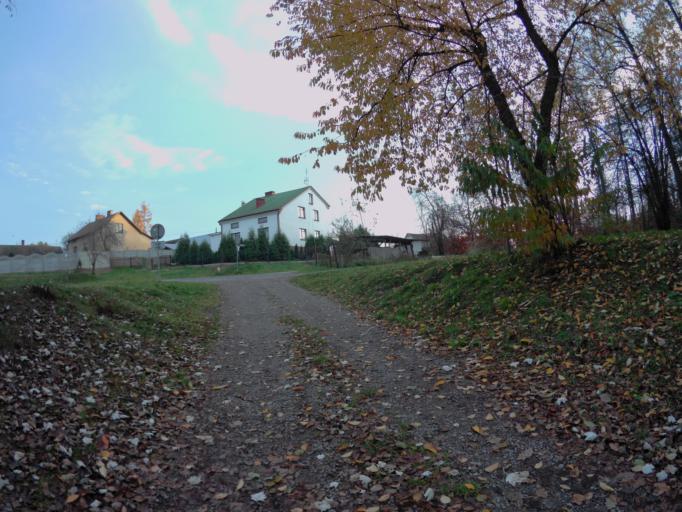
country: PL
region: Subcarpathian Voivodeship
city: Nowa Sarzyna
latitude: 50.3140
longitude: 22.3368
